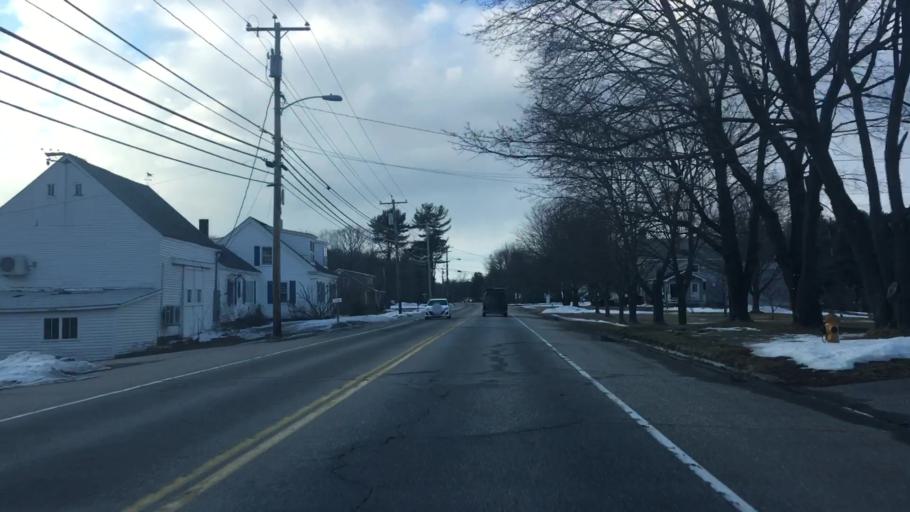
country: US
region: Maine
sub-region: York County
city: Saco
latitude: 43.4798
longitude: -70.4239
